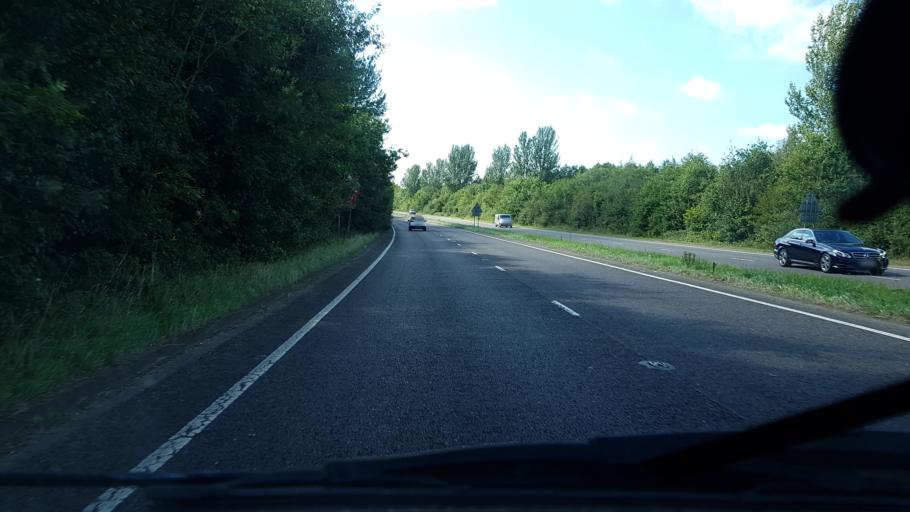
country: GB
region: England
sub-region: West Sussex
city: Horsham
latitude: 51.0867
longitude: -0.2969
